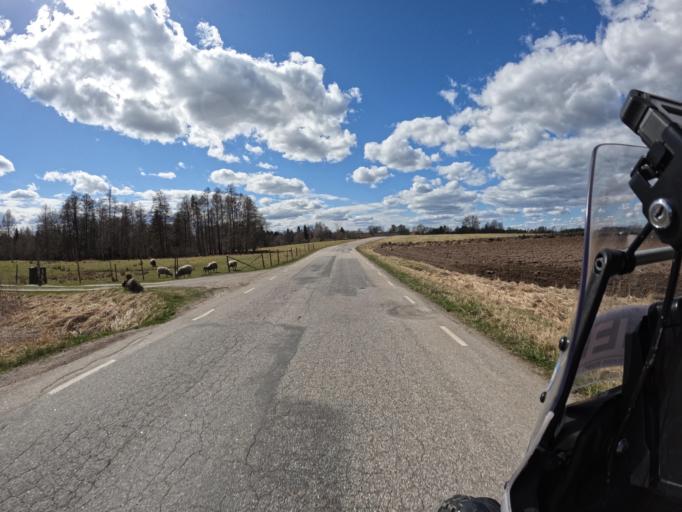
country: SE
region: Vaestra Goetaland
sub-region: Falkopings Kommun
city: Floby
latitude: 57.9668
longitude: 13.3149
